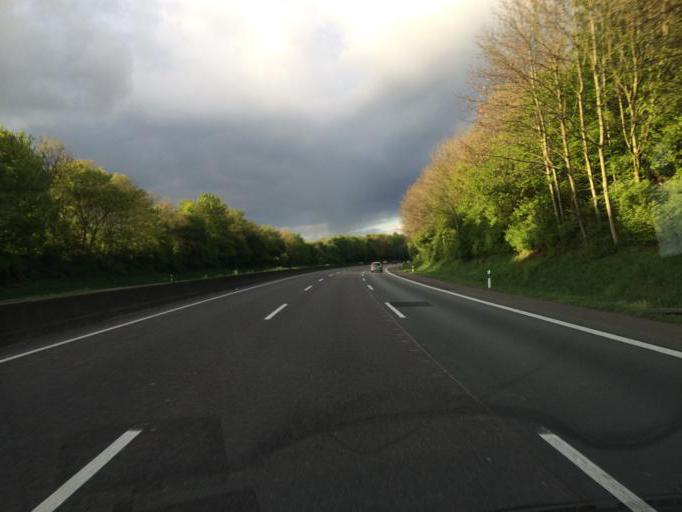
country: DE
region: North Rhine-Westphalia
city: Burscheid
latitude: 51.1039
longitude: 7.1417
